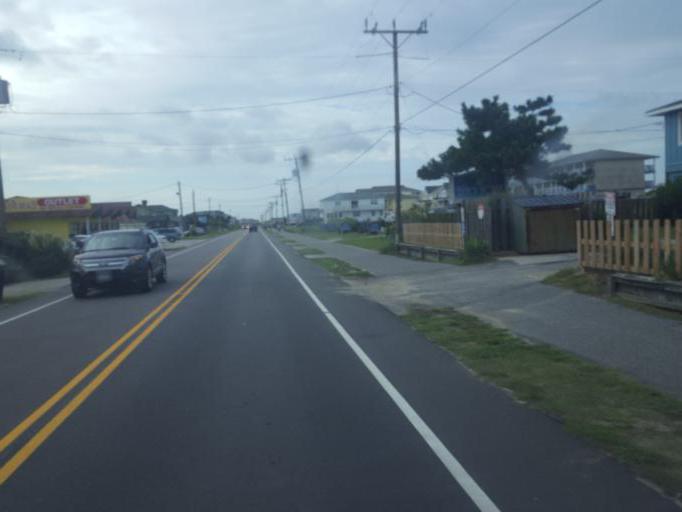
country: US
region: North Carolina
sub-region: Dare County
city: Nags Head
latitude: 35.9166
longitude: -75.6013
